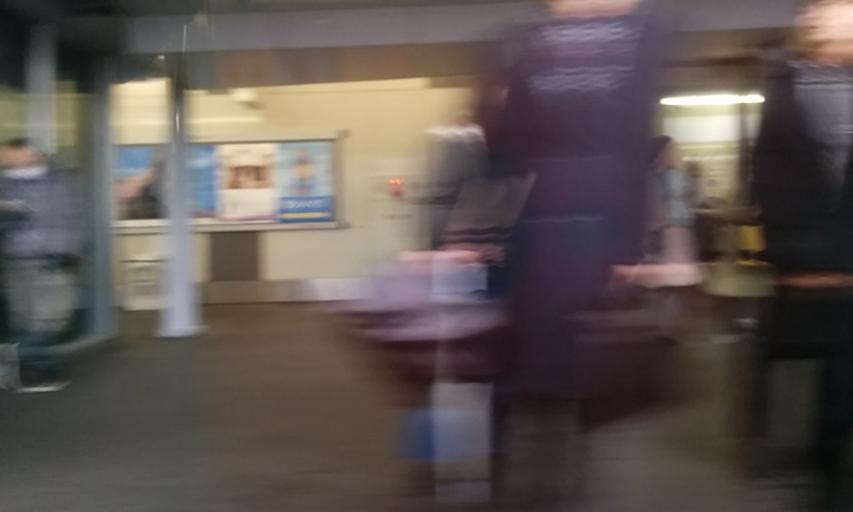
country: JP
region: Tokyo
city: Tokyo
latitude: 35.6684
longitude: 139.6508
